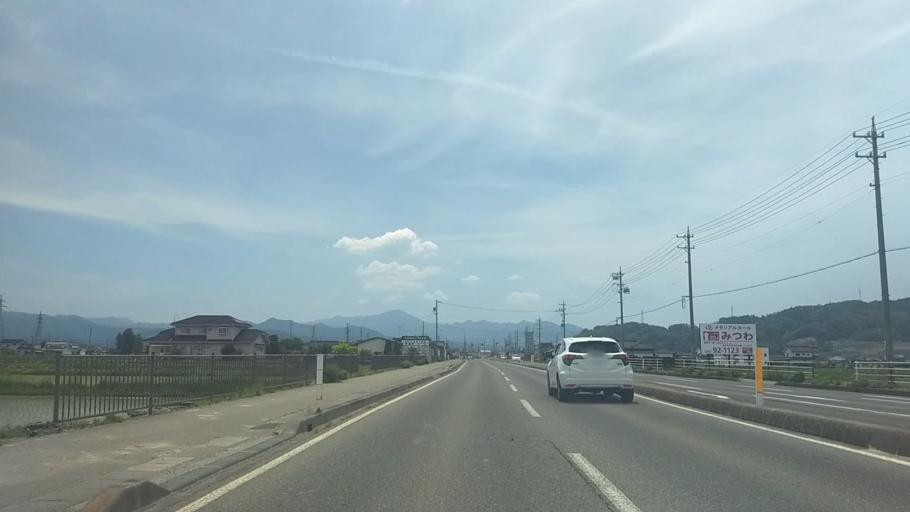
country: JP
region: Nagano
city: Saku
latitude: 36.2161
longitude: 138.4625
